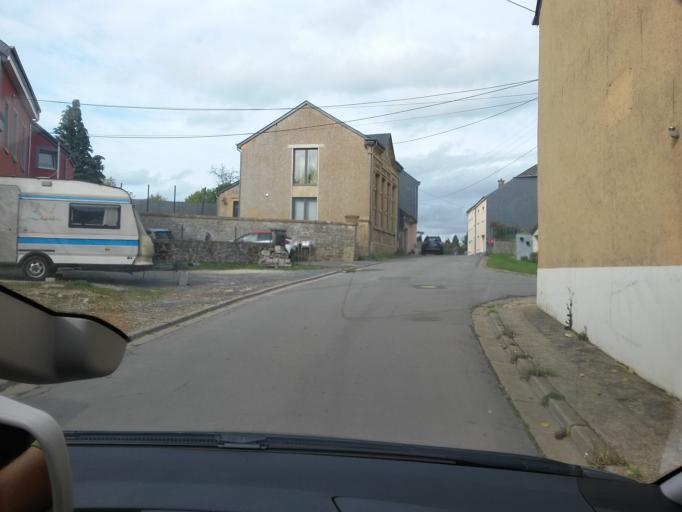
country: BE
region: Wallonia
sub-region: Province du Luxembourg
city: Arlon
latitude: 49.6964
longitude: 5.7916
